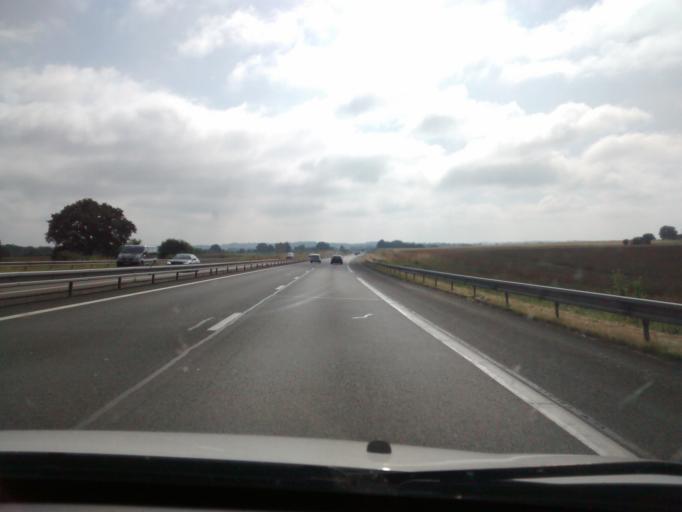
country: FR
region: Pays de la Loire
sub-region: Departement de la Sarthe
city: Loue
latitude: 48.0136
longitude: -0.0881
